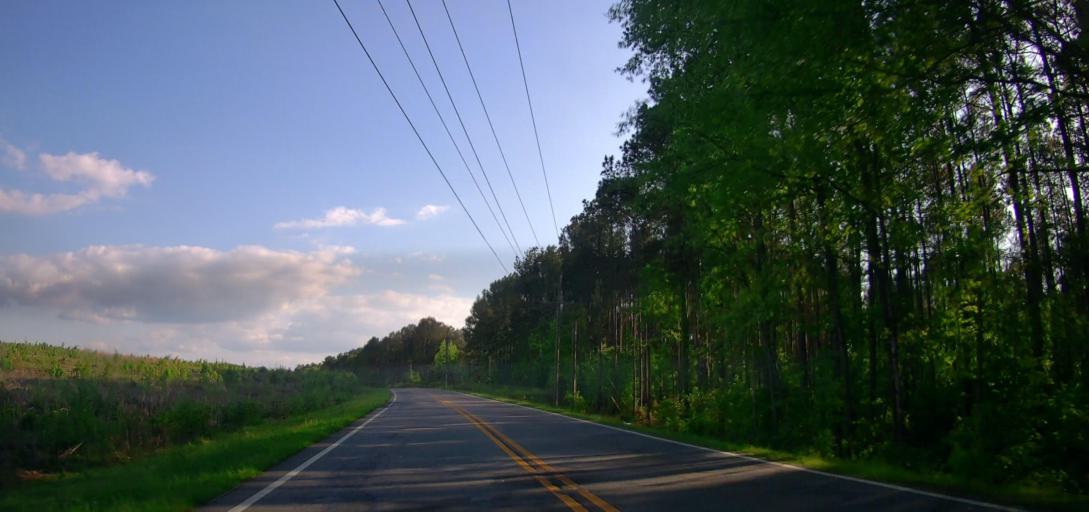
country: US
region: Georgia
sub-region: Putnam County
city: Eatonton
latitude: 33.2524
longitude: -83.3030
